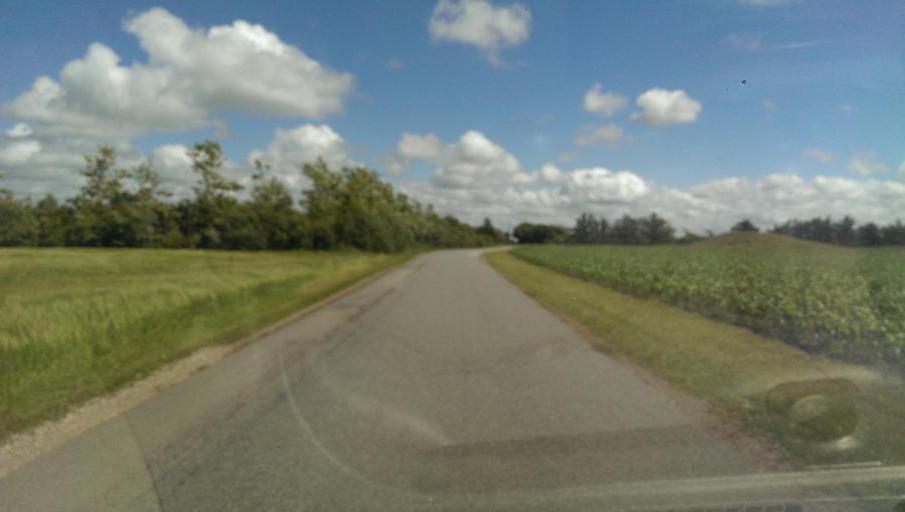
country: DK
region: Central Jutland
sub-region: Holstebro Kommune
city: Ulfborg
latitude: 56.2365
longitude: 8.2121
